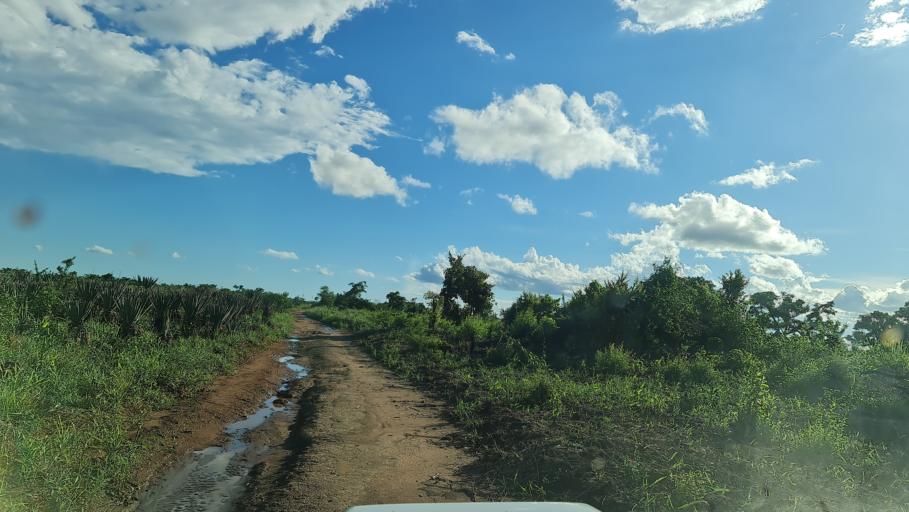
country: MZ
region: Nampula
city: Ilha de Mocambique
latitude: -14.9394
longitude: 40.2006
